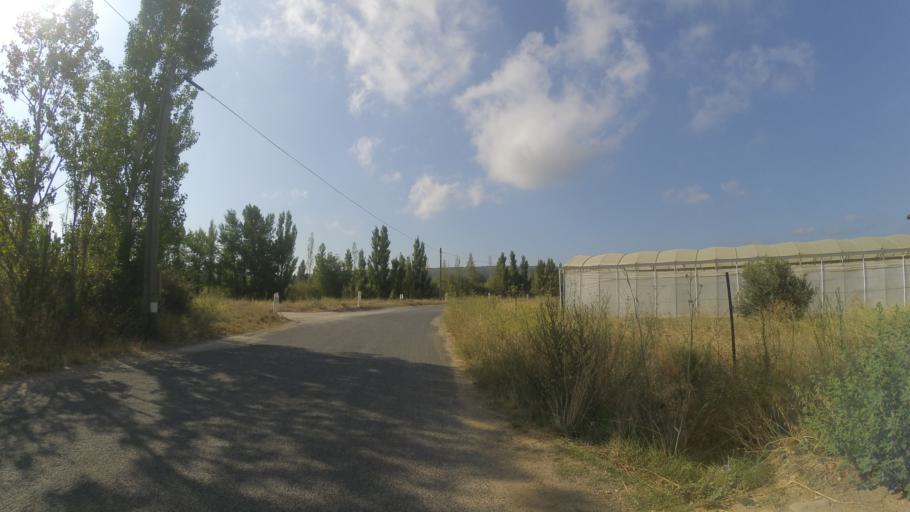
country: FR
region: Languedoc-Roussillon
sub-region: Departement des Pyrenees-Orientales
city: Millas
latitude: 42.6526
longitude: 2.7085
